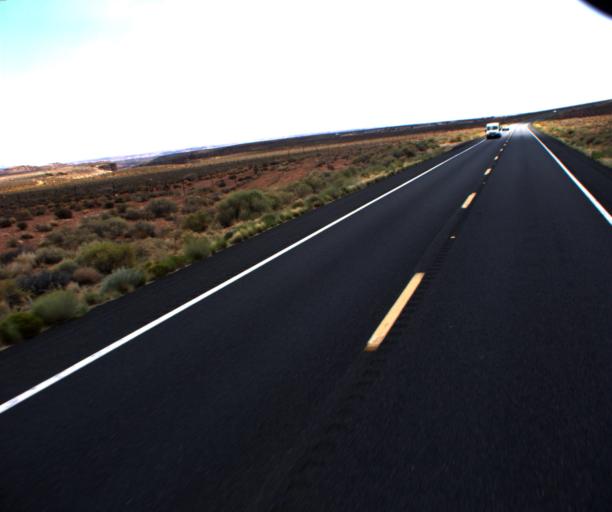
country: US
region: Arizona
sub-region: Coconino County
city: Tuba City
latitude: 35.9208
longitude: -111.5745
